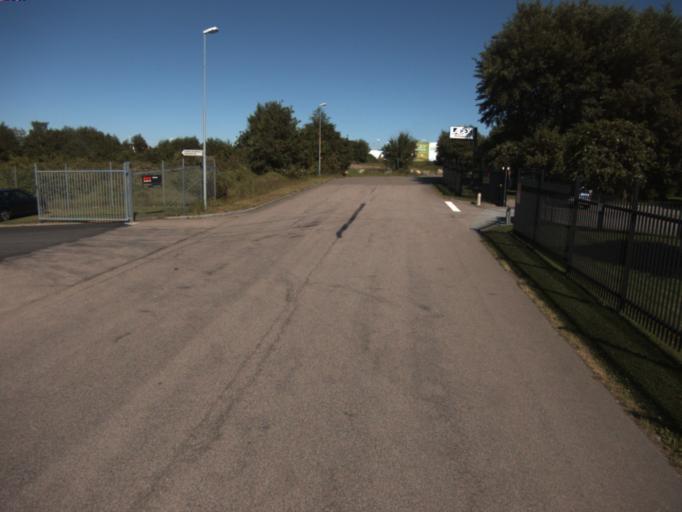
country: SE
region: Skane
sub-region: Helsingborg
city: Odakra
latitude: 56.0919
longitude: 12.7482
